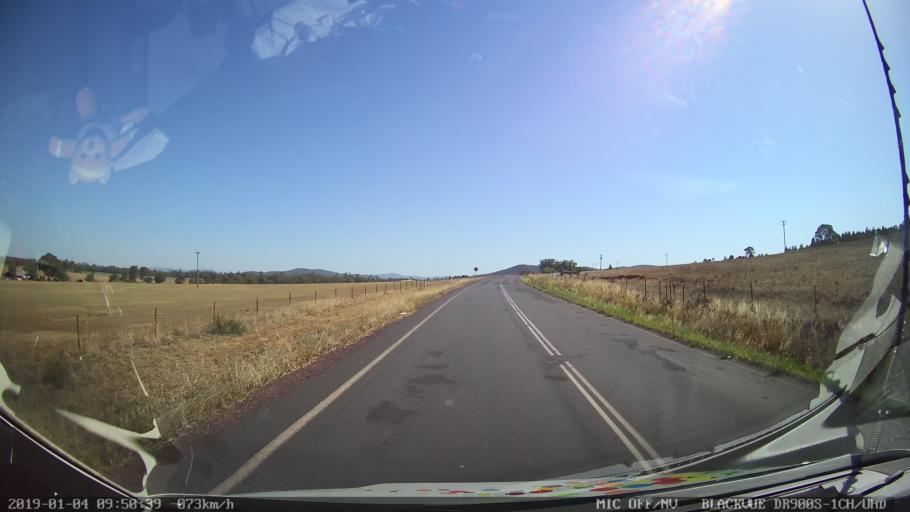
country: AU
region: New South Wales
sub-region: Cabonne
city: Canowindra
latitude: -33.5820
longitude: 148.4161
